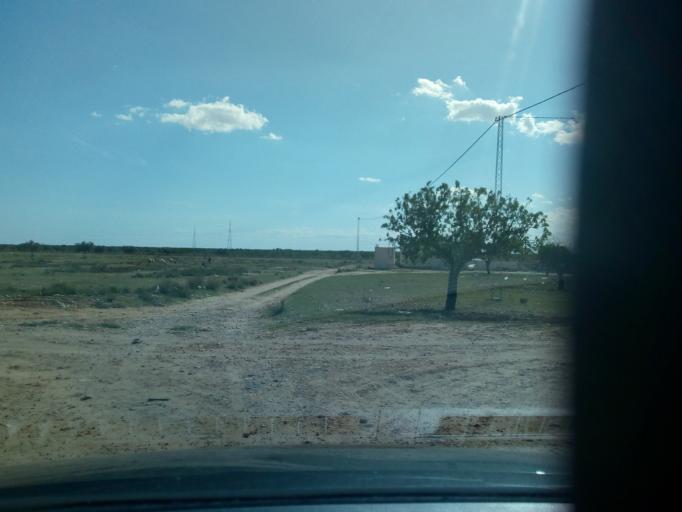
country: TN
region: Safaqis
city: Sfax
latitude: 34.7244
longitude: 10.6023
